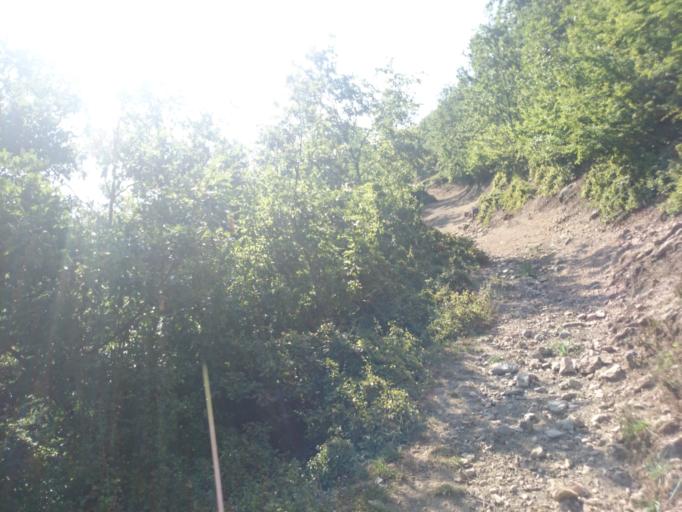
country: AL
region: Diber
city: Peshkopi
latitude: 41.6385
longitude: 20.4082
